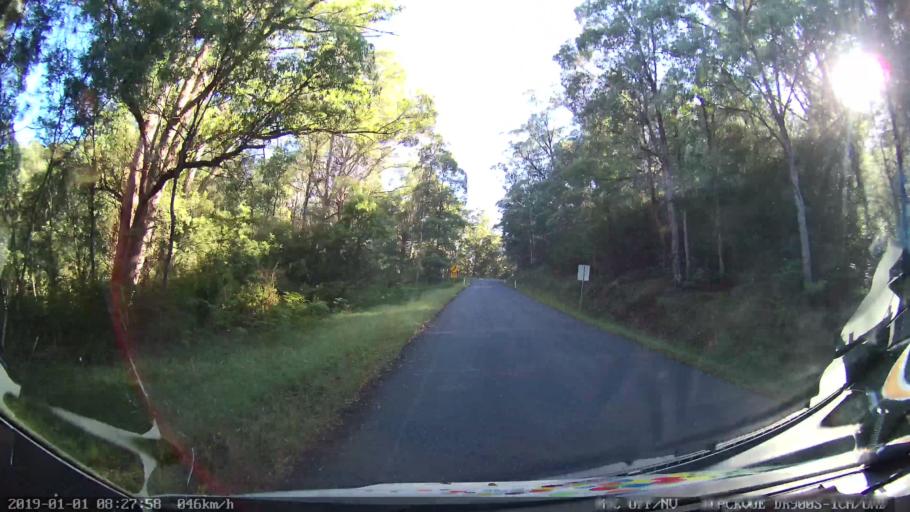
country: AU
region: New South Wales
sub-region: Snowy River
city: Jindabyne
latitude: -36.3785
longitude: 148.1870
